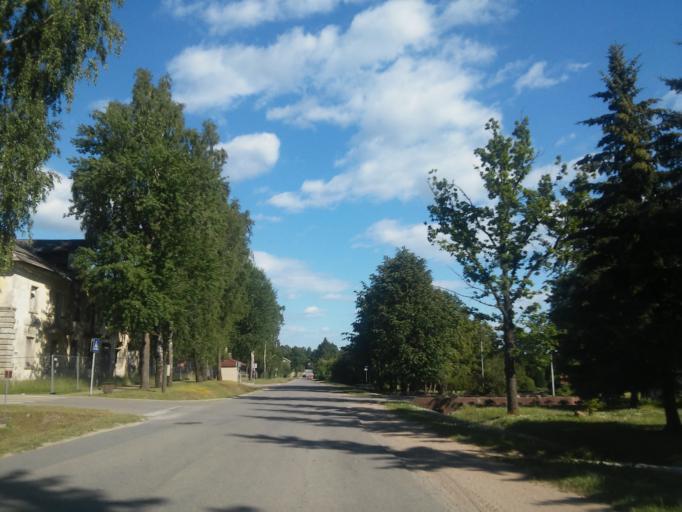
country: LV
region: Vainode
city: Vainode
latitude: 56.4180
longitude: 21.8449
